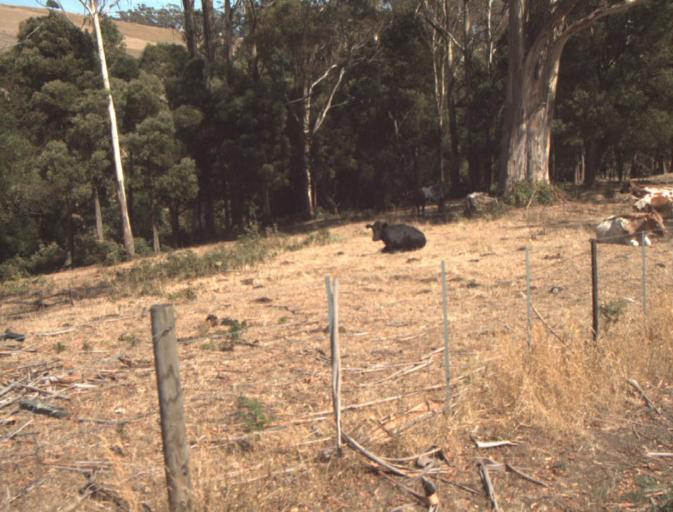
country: AU
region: Tasmania
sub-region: Launceston
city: Mayfield
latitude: -41.2335
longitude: 147.2549
